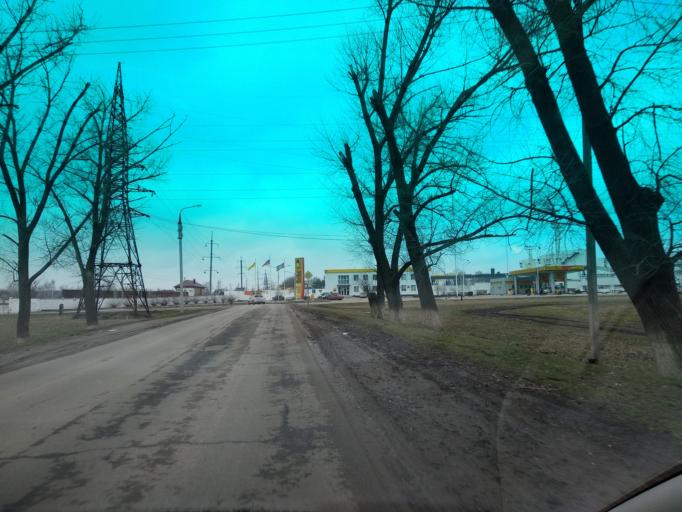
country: RU
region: Krasnodarskiy
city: Tikhoretsk
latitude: 45.8391
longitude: 40.1248
